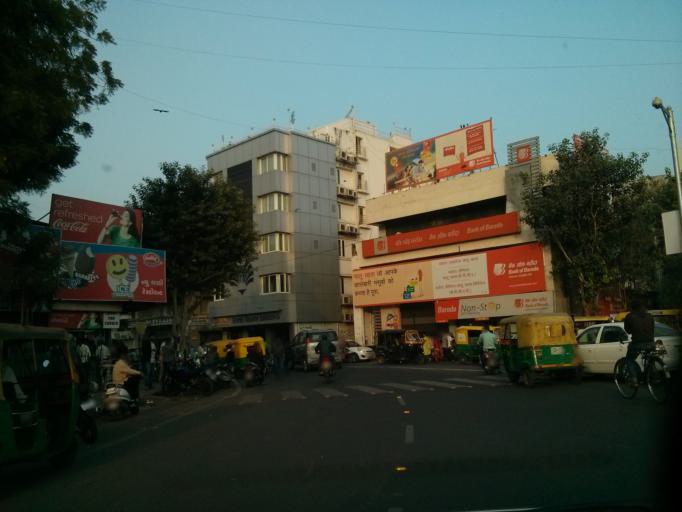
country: IN
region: Gujarat
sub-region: Ahmadabad
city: Ahmedabad
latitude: 23.0275
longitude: 72.5811
